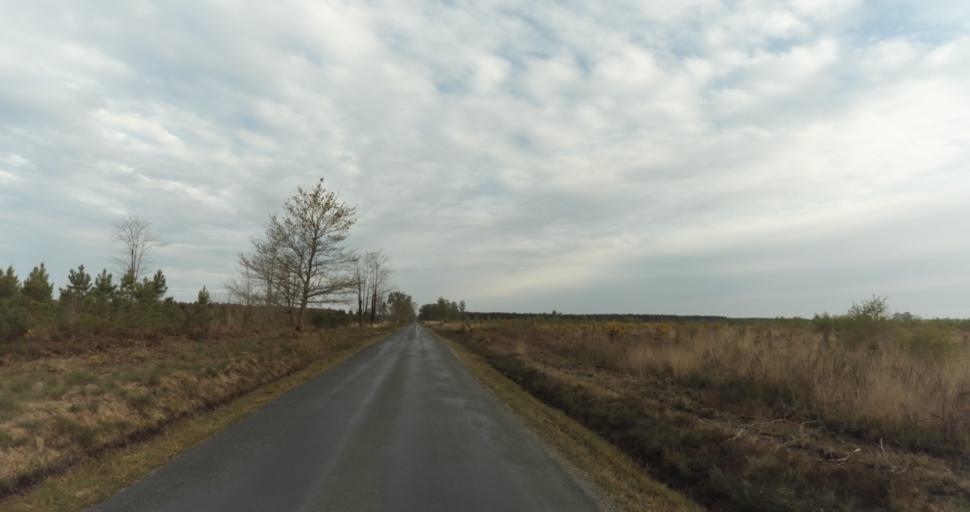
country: FR
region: Aquitaine
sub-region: Departement de la Gironde
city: Saint-Aubin-de-Medoc
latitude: 44.7817
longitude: -0.7472
